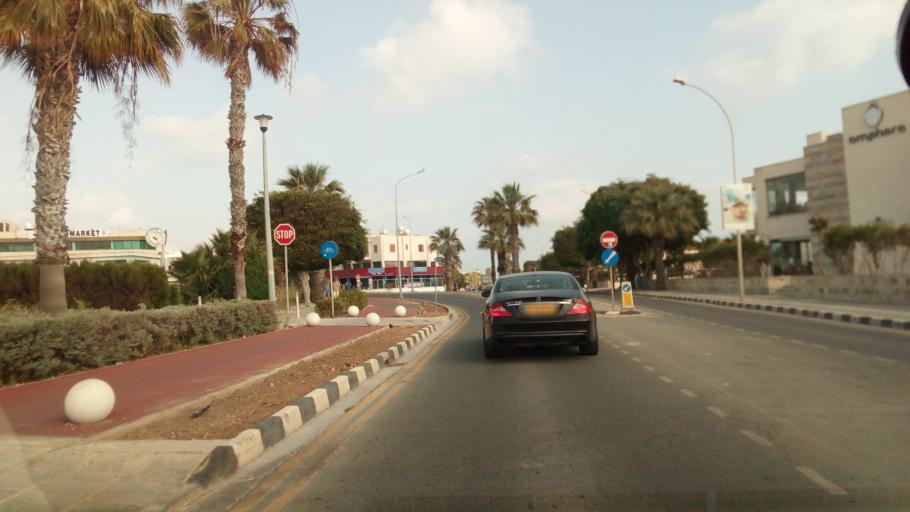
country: CY
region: Pafos
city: Paphos
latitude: 34.7488
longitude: 32.4245
